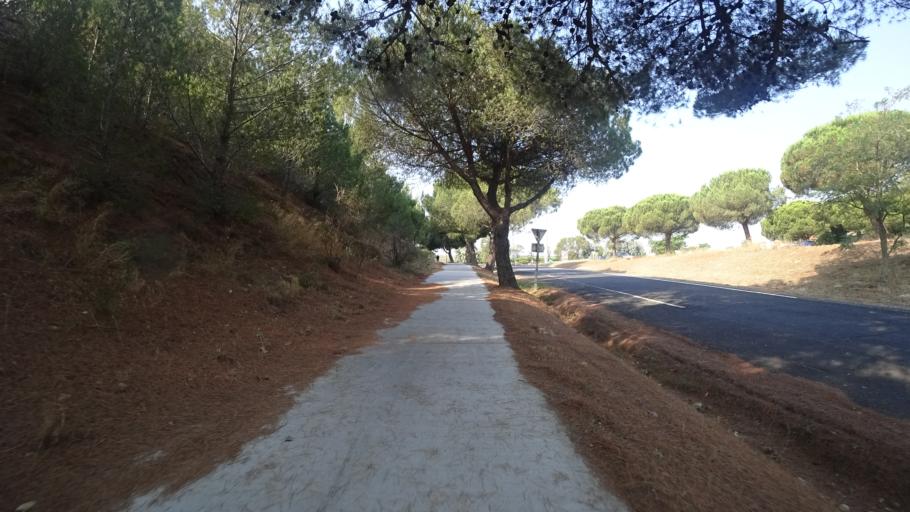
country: FR
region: Languedoc-Roussillon
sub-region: Departement des Pyrenees-Orientales
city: Canet-en-Roussillon
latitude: 42.7042
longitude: 3.0173
